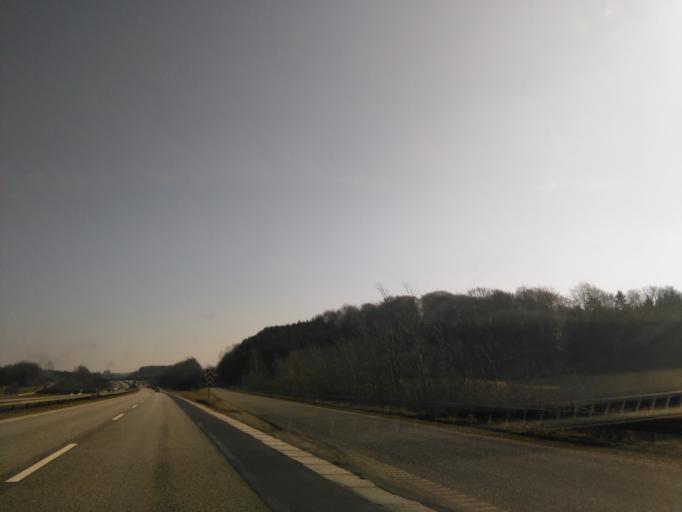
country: DK
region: South Denmark
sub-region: Assens Kommune
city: Vissenbjerg
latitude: 55.4028
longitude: 10.1497
